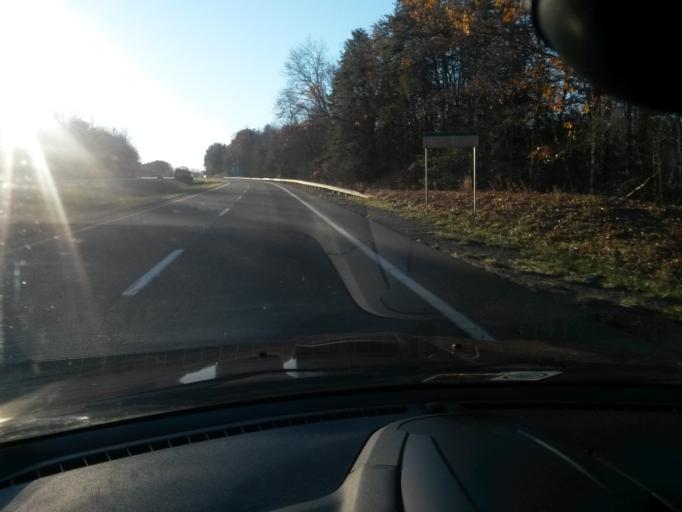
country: US
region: Virginia
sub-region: Henry County
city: Horse Pasture
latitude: 36.6526
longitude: -79.9209
